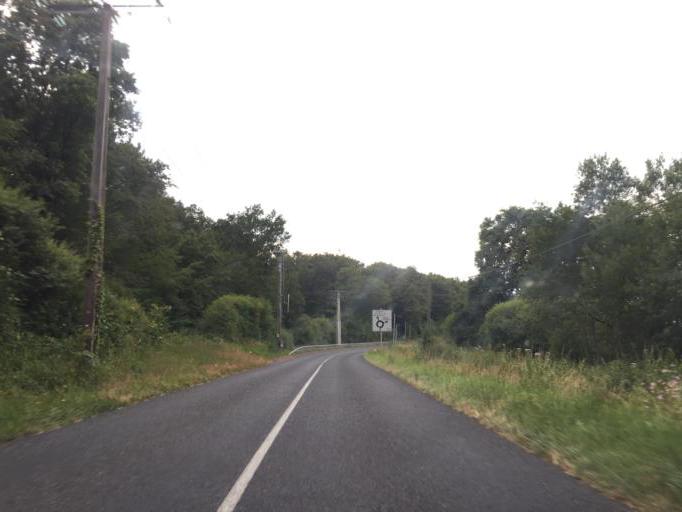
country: FR
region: Auvergne
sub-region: Departement de l'Allier
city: Lusigny
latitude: 46.5342
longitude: 3.4470
